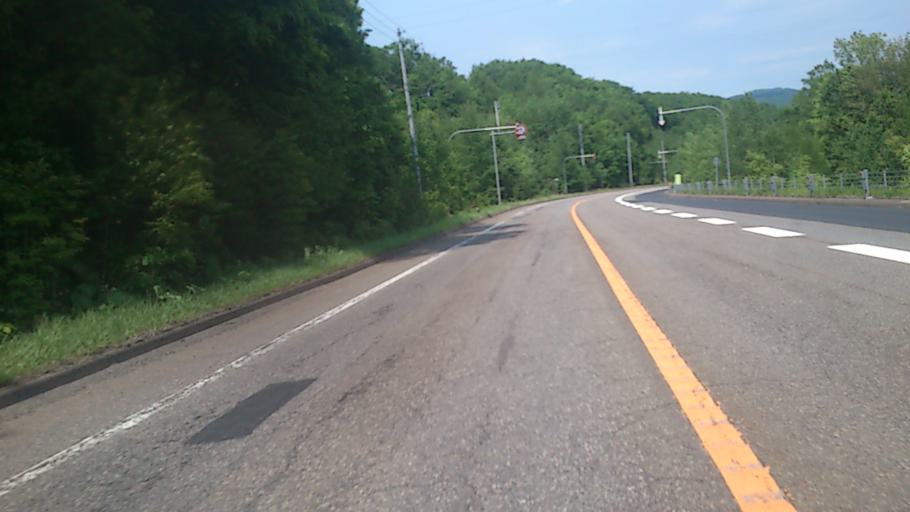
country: JP
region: Hokkaido
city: Otofuke
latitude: 43.2328
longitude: 143.5262
